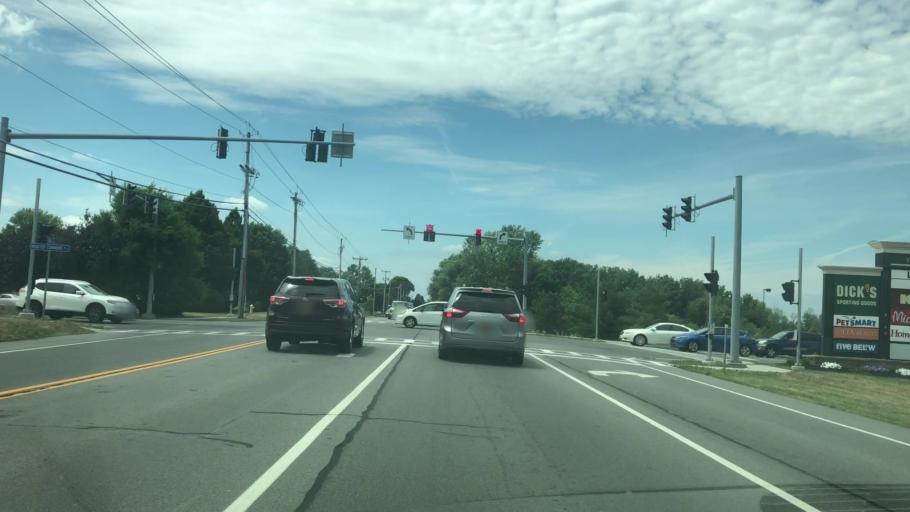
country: US
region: New York
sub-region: Monroe County
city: Webster
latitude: 43.2100
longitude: -77.4513
